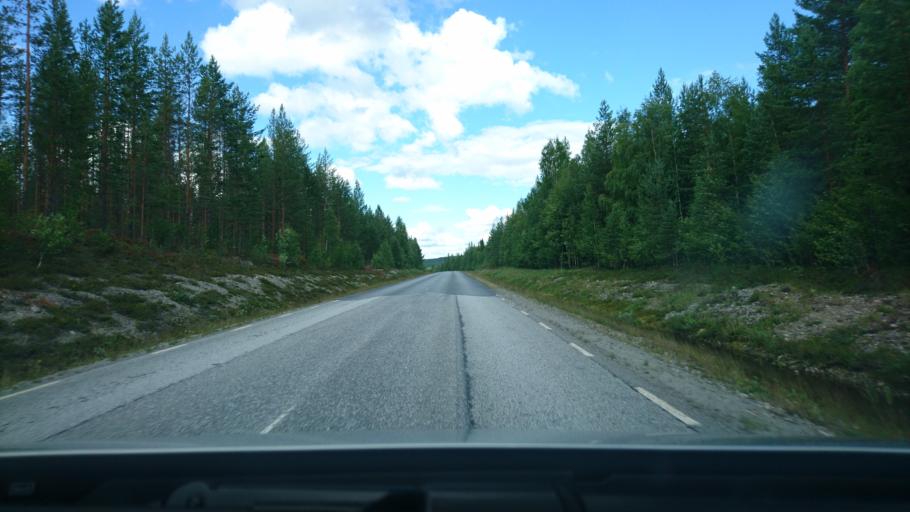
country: SE
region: Vaesterbotten
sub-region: Asele Kommun
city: Asele
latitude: 64.0758
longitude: 17.2997
